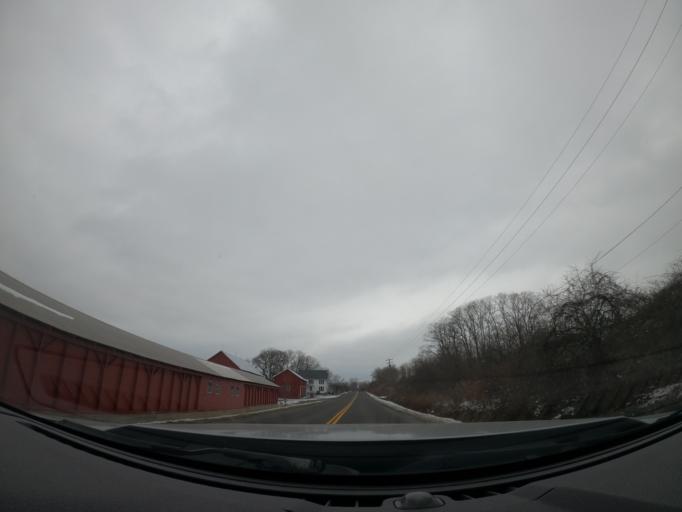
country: US
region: New York
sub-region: Cayuga County
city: Moravia
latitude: 42.7429
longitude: -76.3829
